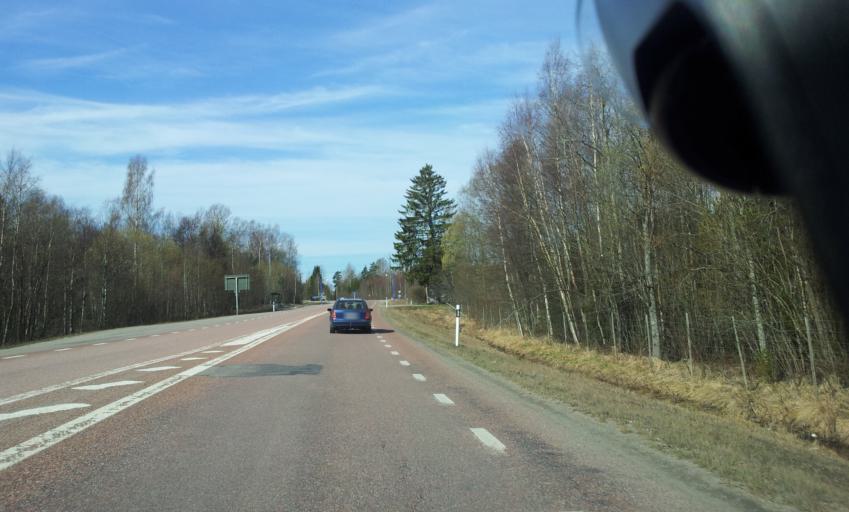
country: SE
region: Gaevleborg
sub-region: Hudiksvalls Kommun
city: Hudiksvall
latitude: 61.7142
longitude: 17.0676
